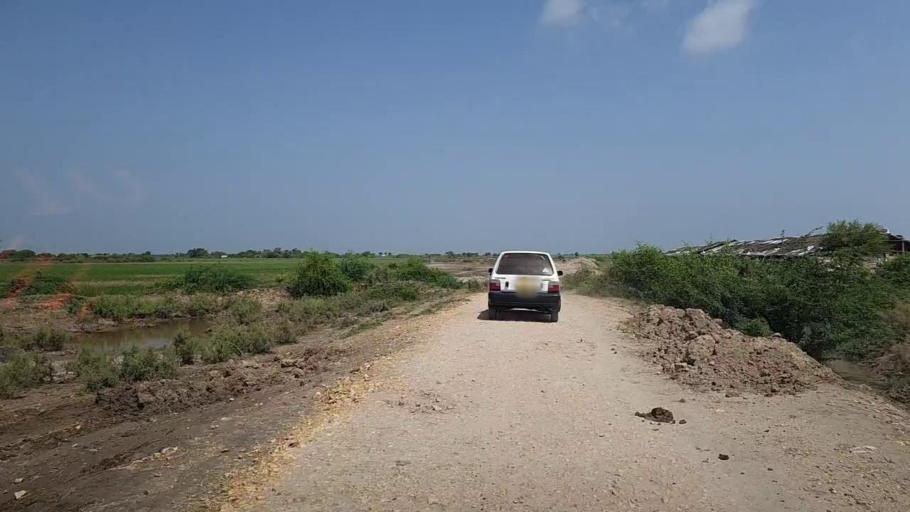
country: PK
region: Sindh
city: Mirpur Batoro
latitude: 24.6512
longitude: 68.4245
